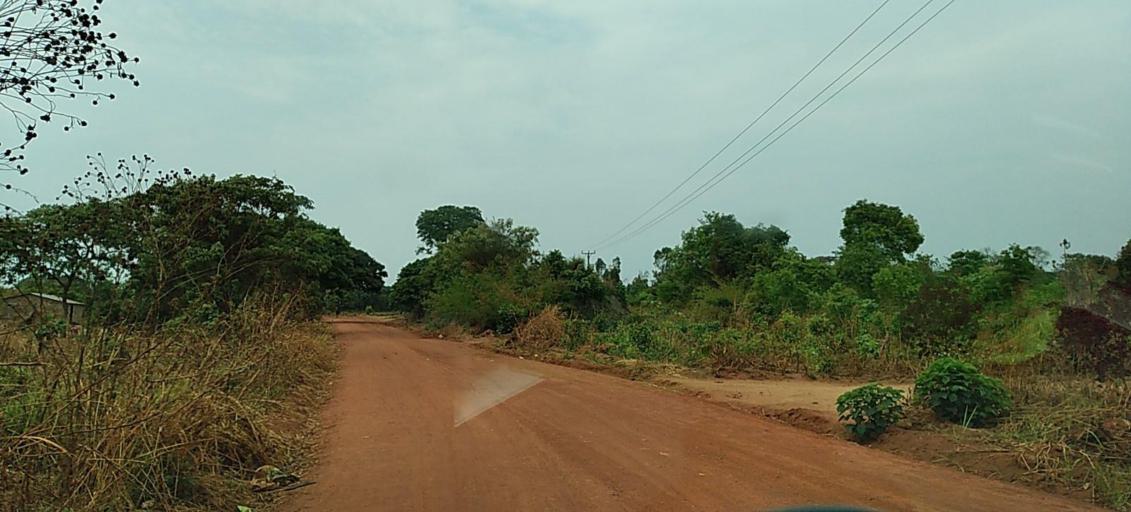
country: ZM
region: North-Western
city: Solwezi
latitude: -12.2432
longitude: 26.5118
